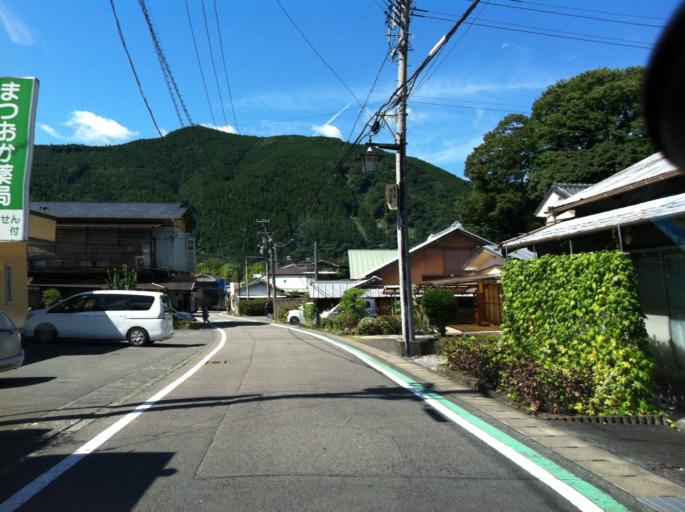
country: JP
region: Shizuoka
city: Kanaya
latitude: 35.0757
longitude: 138.1127
